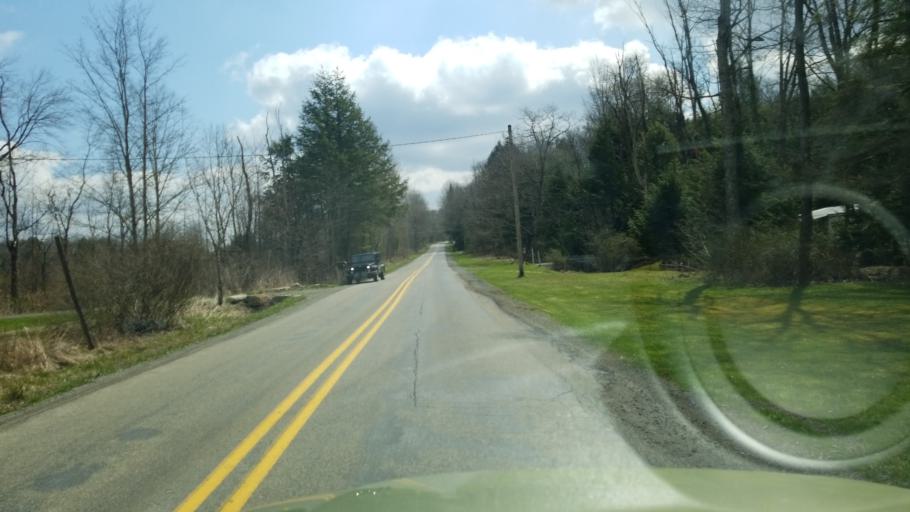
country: US
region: Pennsylvania
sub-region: Jefferson County
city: Brockway
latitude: 41.2790
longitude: -78.8482
